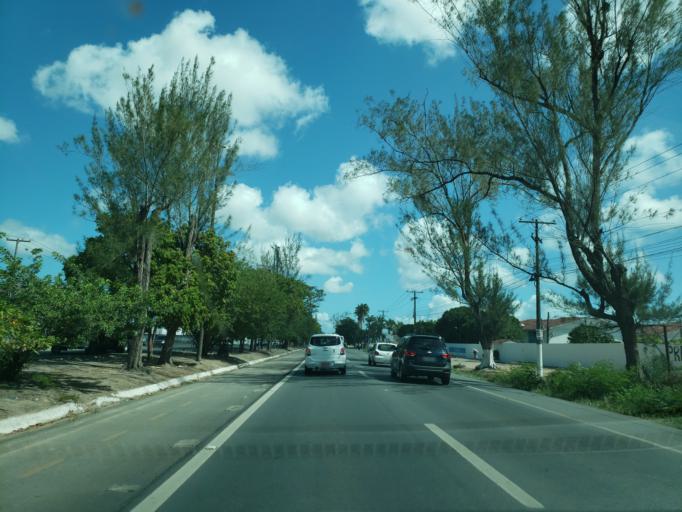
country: BR
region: Alagoas
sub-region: Satuba
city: Satuba
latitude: -9.5486
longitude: -35.7867
